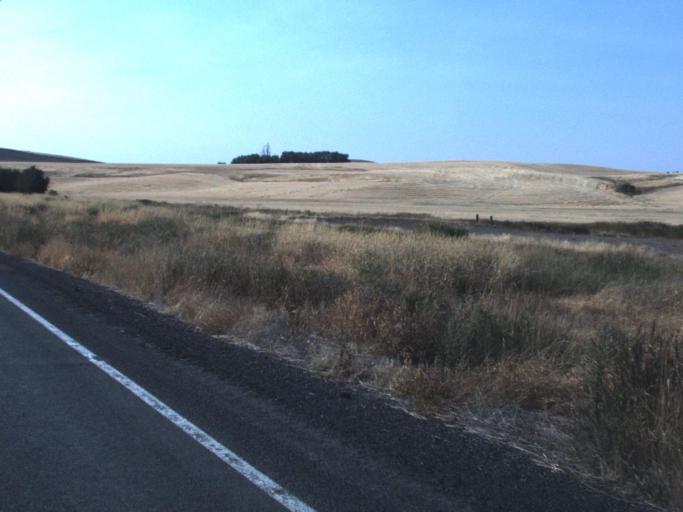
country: US
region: Idaho
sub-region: Benewah County
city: Plummer
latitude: 47.2483
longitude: -117.1328
